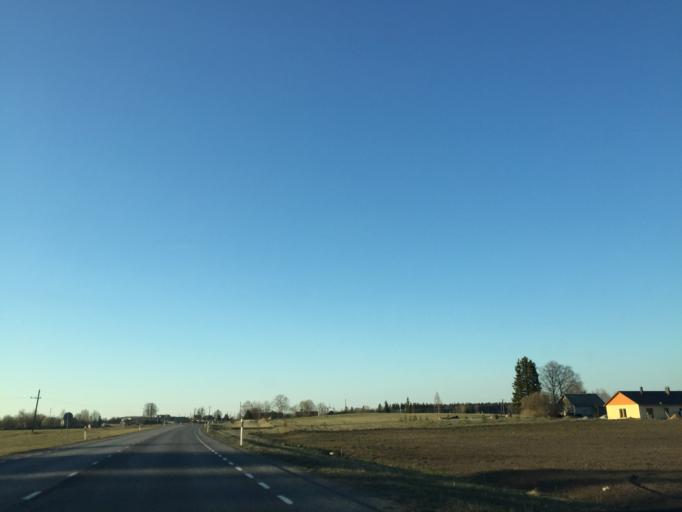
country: EE
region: Ida-Virumaa
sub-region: Johvi vald
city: Johvi
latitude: 59.2959
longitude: 27.4951
